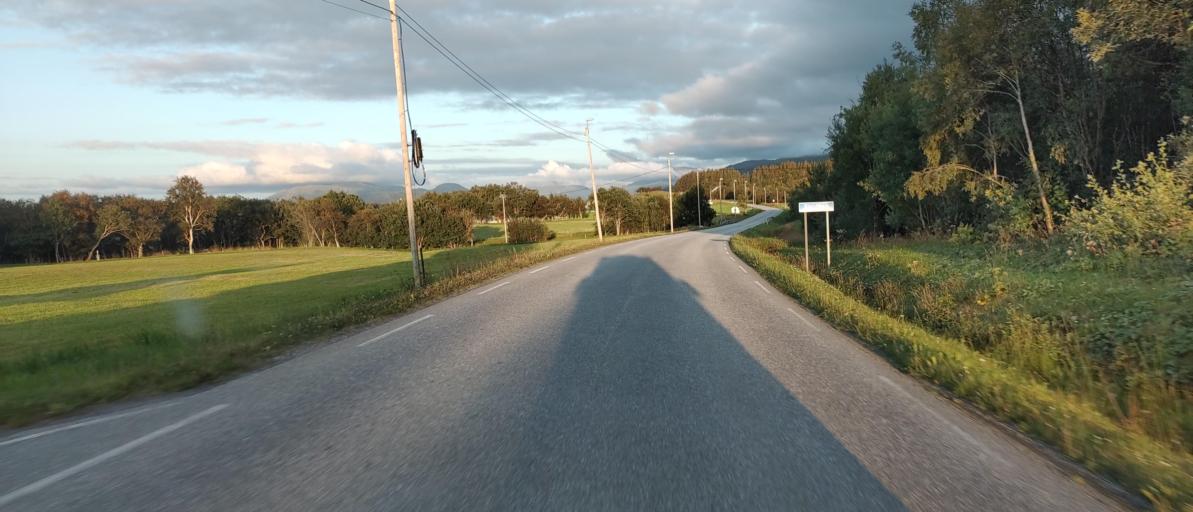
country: NO
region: More og Romsdal
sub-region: Fraena
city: Elnesvagen
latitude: 62.9913
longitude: 7.1959
